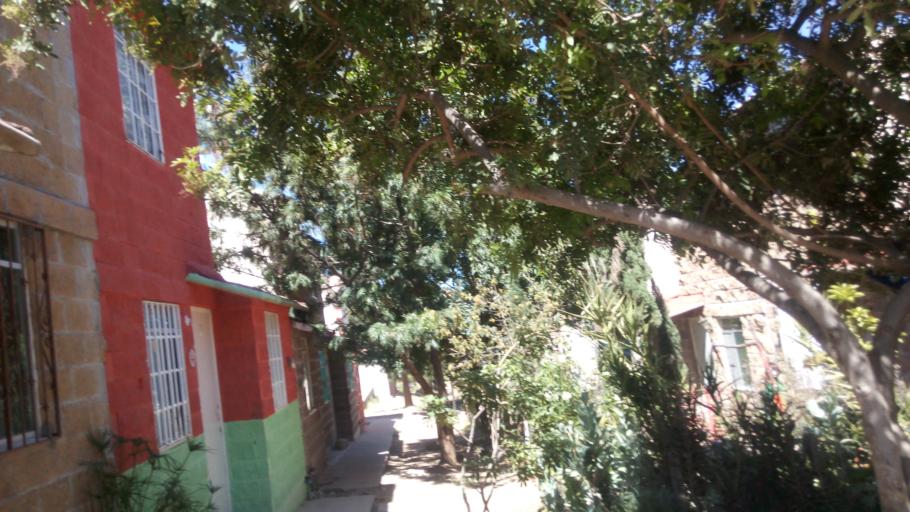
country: MX
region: Aguascalientes
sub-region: Aguascalientes
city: Aguascalientes
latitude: 21.8741
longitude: -102.2360
